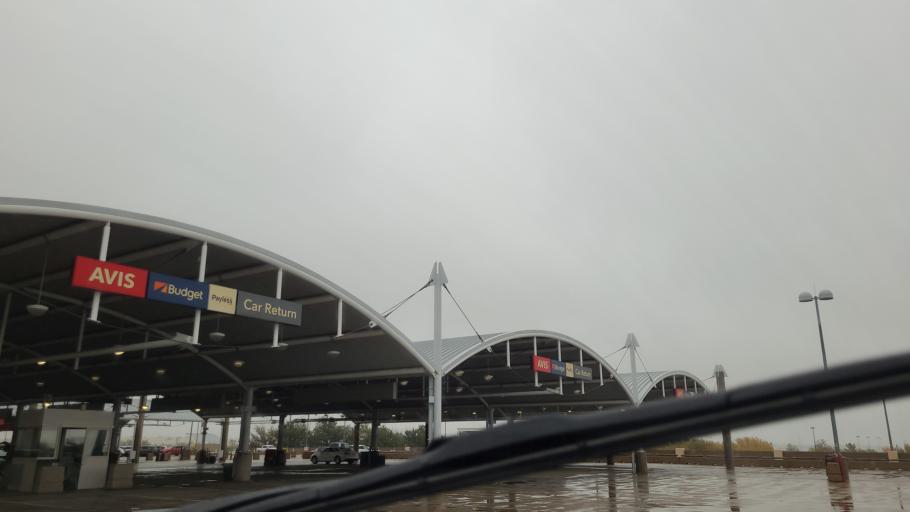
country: US
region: Texas
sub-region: Tarrant County
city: Euless
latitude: 32.8563
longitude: -97.0350
